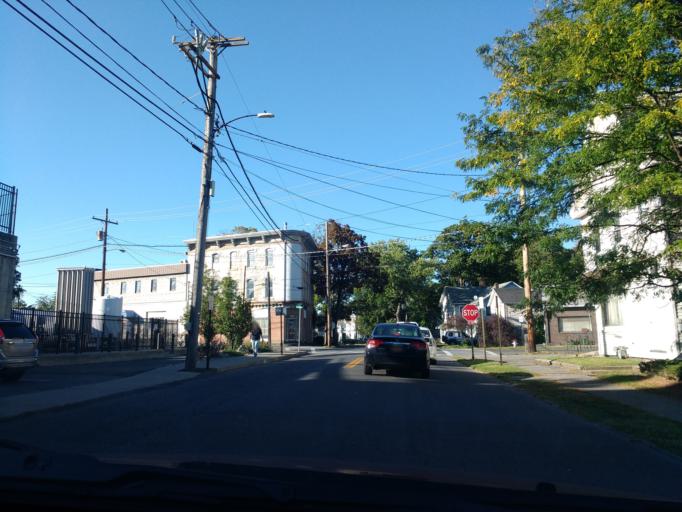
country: US
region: New York
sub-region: Ulster County
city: Kingston
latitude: 41.9272
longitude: -73.9943
